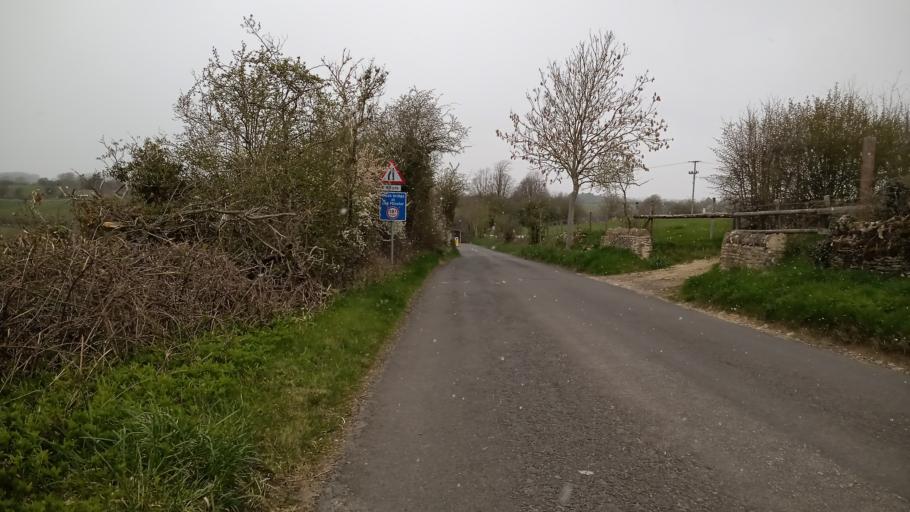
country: GB
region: England
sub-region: Oxfordshire
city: Witney
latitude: 51.8035
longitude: -1.5055
